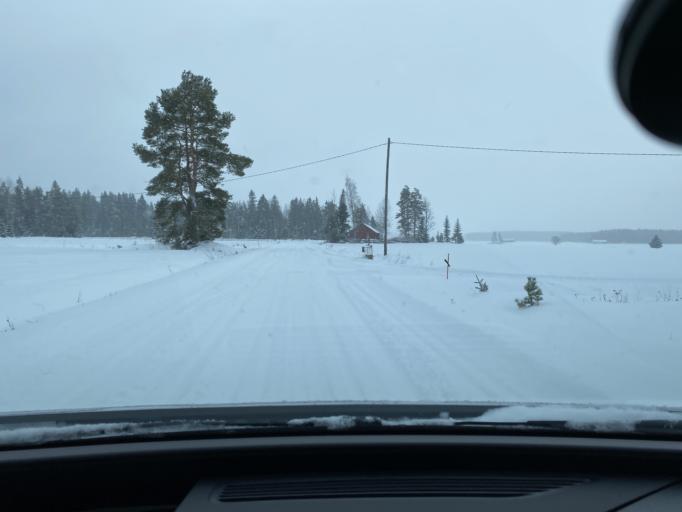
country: FI
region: Haeme
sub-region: Forssa
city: Humppila
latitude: 61.0114
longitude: 23.3031
